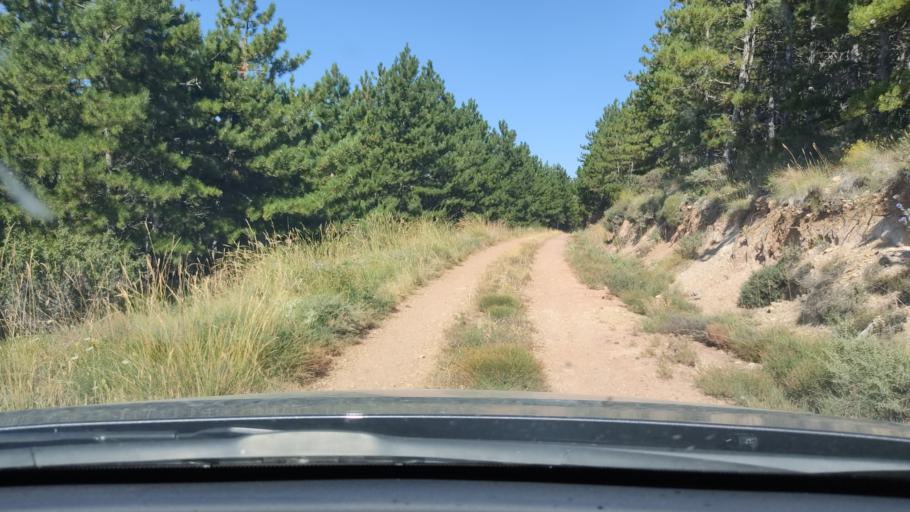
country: ES
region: Aragon
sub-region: Provincia de Teruel
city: Monforte de Moyuela
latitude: 41.0329
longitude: -1.0448
